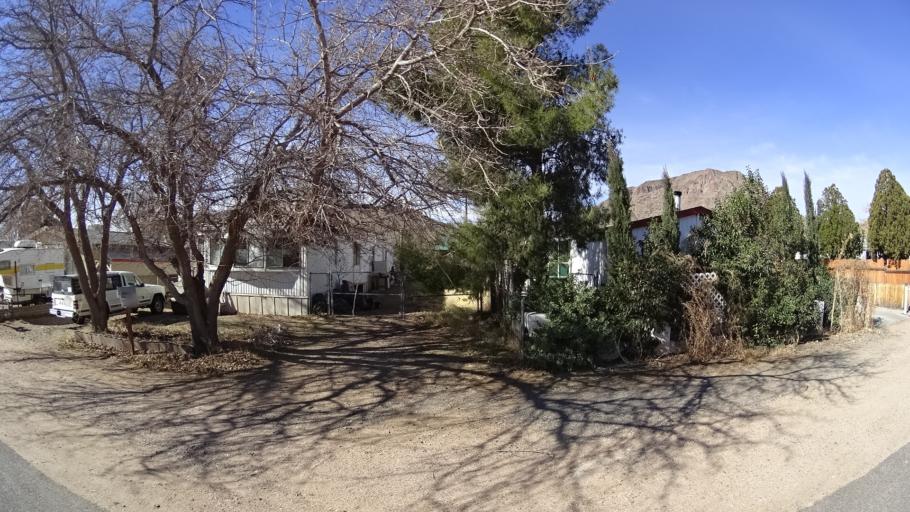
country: US
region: Arizona
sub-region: Mohave County
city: New Kingman-Butler
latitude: 35.2692
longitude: -114.0422
